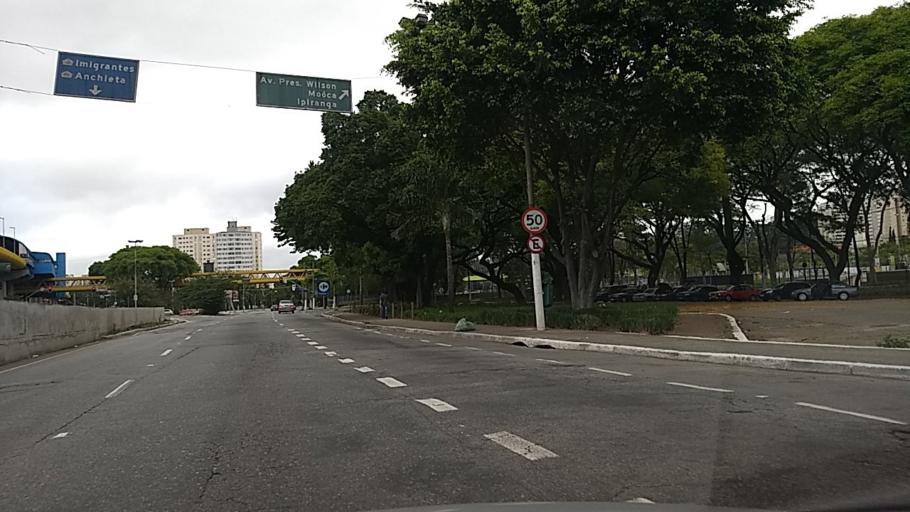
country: BR
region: Sao Paulo
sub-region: Sao Paulo
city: Sao Paulo
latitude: -23.5626
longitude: -46.6123
